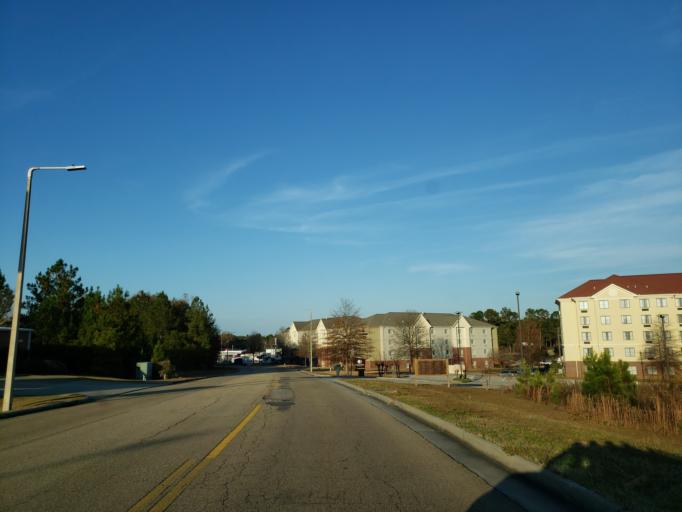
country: US
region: Mississippi
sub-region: Lamar County
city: Arnold Line
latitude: 31.3561
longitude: -89.3507
